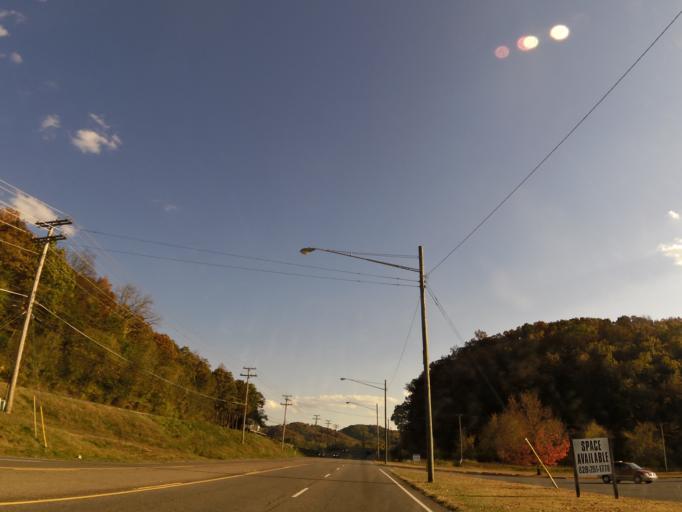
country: US
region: Tennessee
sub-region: Anderson County
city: Clinton
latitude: 36.0913
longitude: -84.1297
